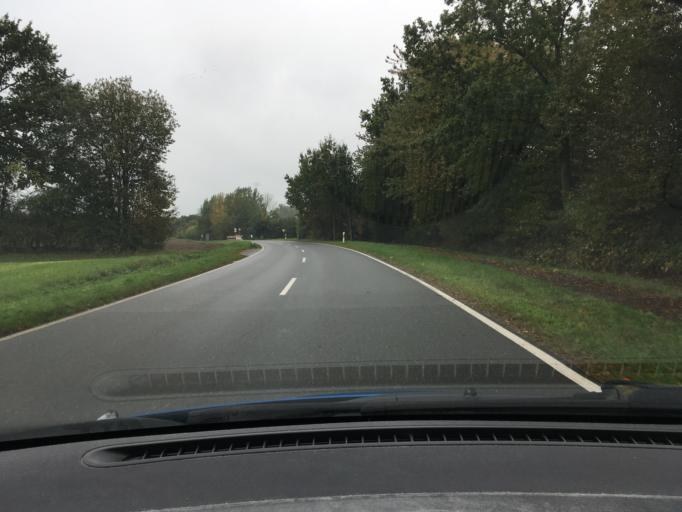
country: DE
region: Schleswig-Holstein
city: Bosdorf
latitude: 54.1058
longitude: 10.4789
